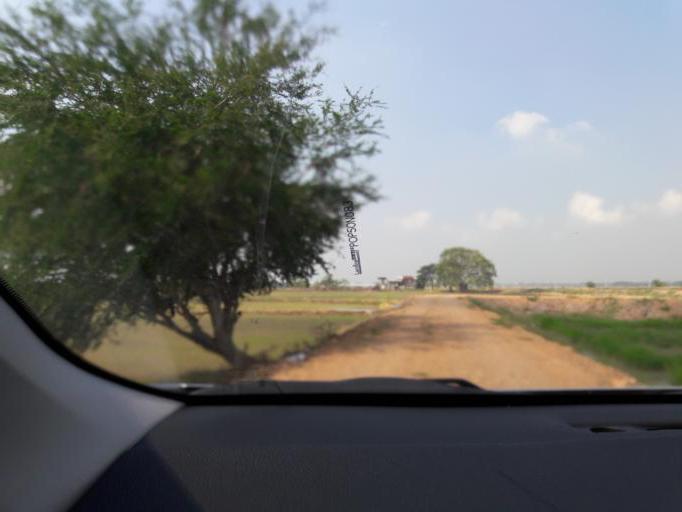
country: TH
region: Ang Thong
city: Ang Thong
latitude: 14.5623
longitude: 100.4125
